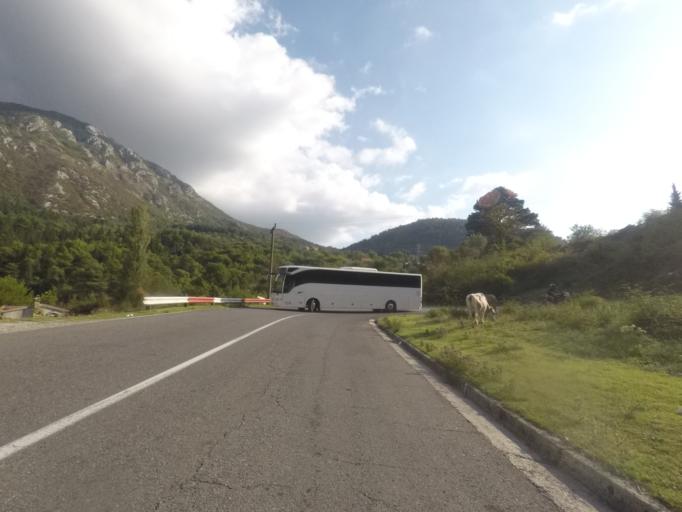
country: ME
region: Kotor
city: Kotor
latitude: 42.4056
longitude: 18.7649
